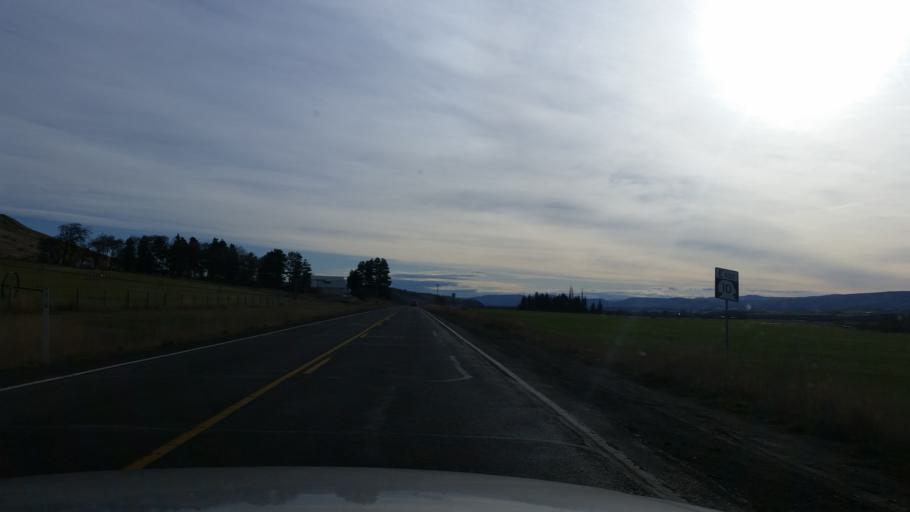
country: US
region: Washington
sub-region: Kittitas County
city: Ellensburg
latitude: 47.1080
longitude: -120.7131
